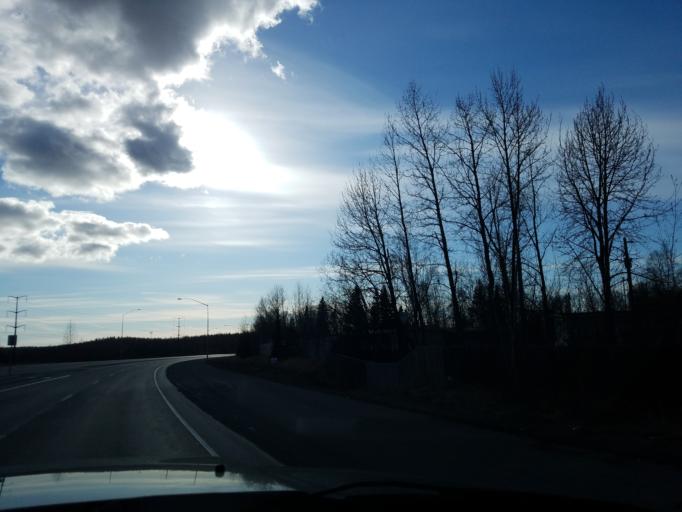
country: US
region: Alaska
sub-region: Anchorage Municipality
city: Elmendorf Air Force Base
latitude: 61.1815
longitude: -149.7403
